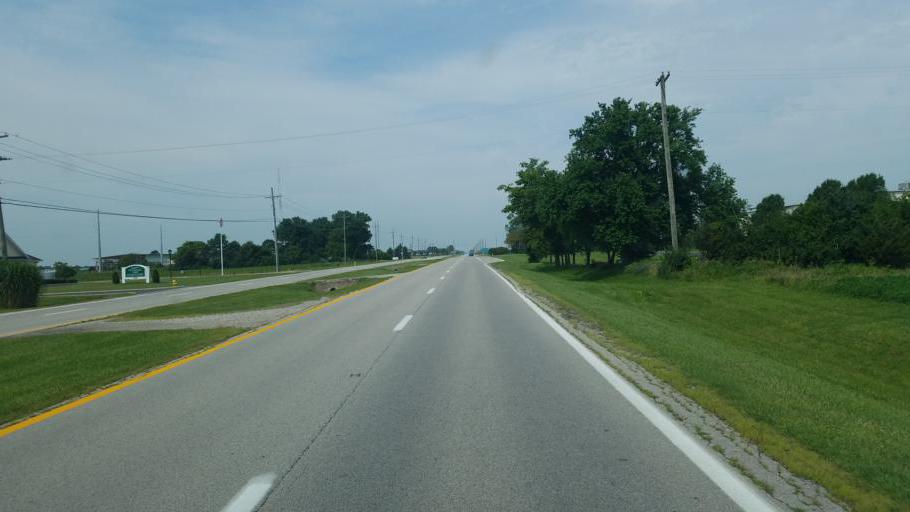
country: US
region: Ohio
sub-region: Madison County
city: West Jefferson
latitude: 39.9431
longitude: -83.3015
